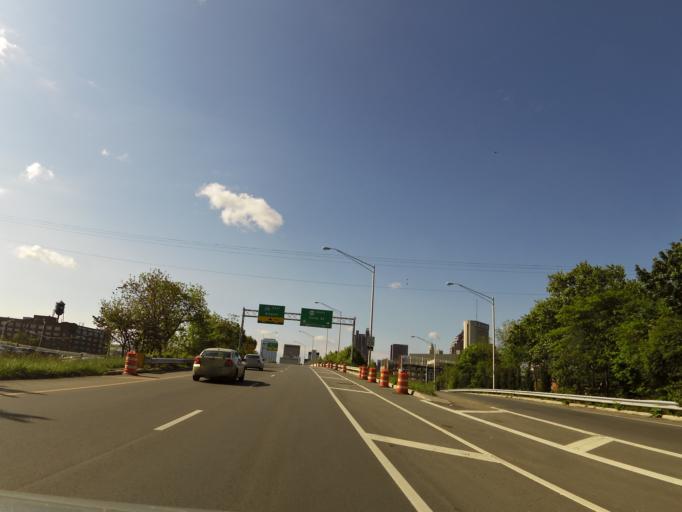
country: US
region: Ohio
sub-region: Franklin County
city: Columbus
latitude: 39.9775
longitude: -83.0003
